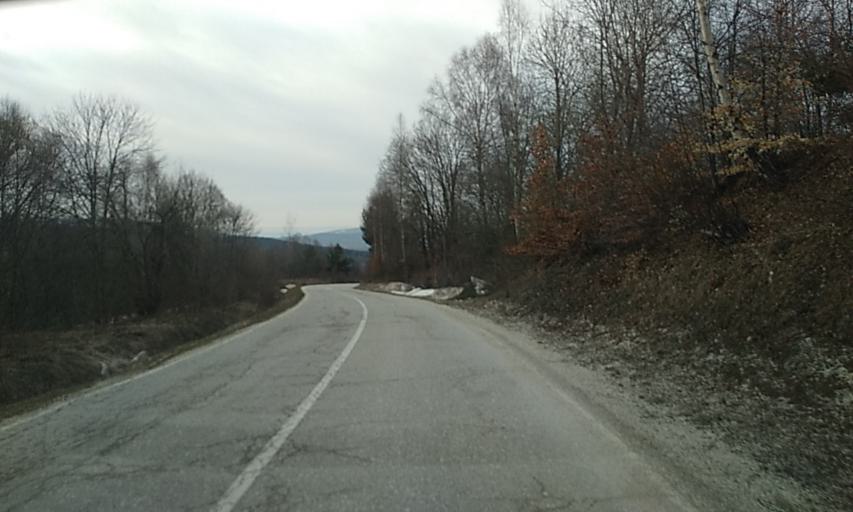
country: RS
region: Central Serbia
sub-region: Jablanicki Okrug
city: Crna Trava
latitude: 42.6736
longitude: 22.3751
